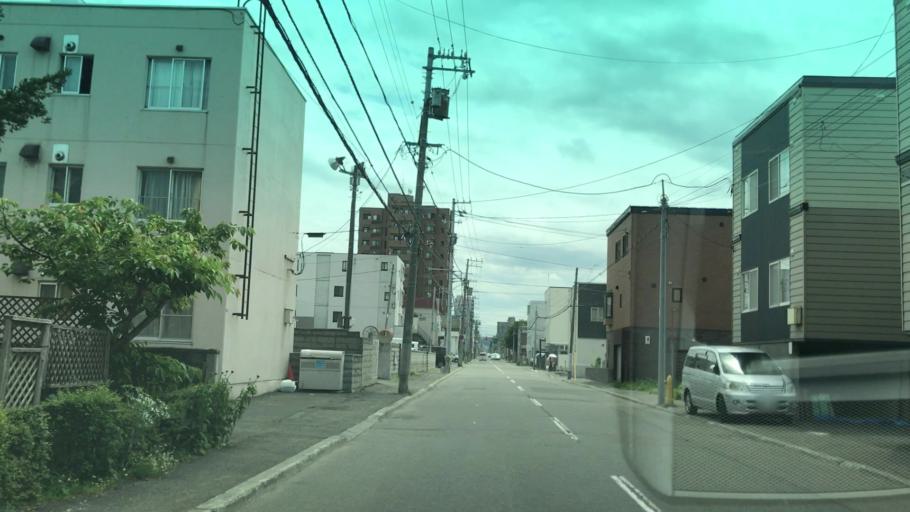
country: JP
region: Hokkaido
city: Sapporo
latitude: 43.0469
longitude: 141.3414
